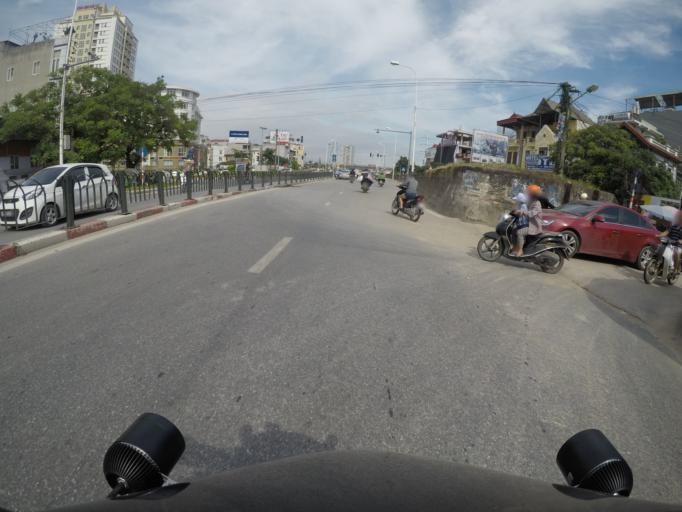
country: VN
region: Ha Noi
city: Tay Ho
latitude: 21.0807
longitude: 105.8185
